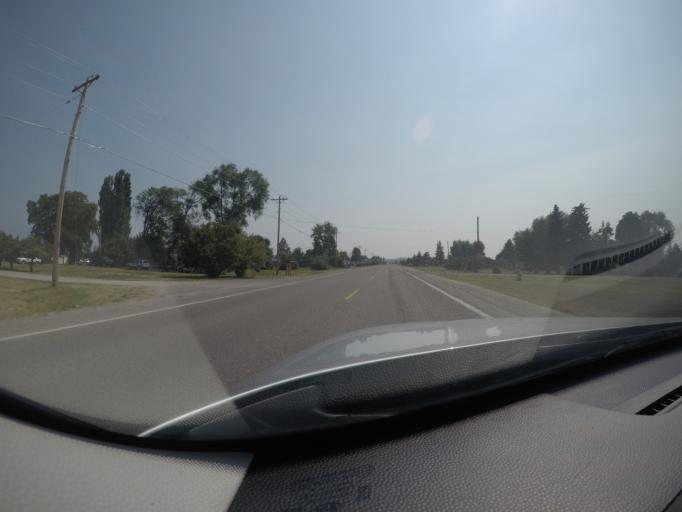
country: US
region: Montana
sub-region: Lake County
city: Polson
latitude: 47.7247
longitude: -114.1885
